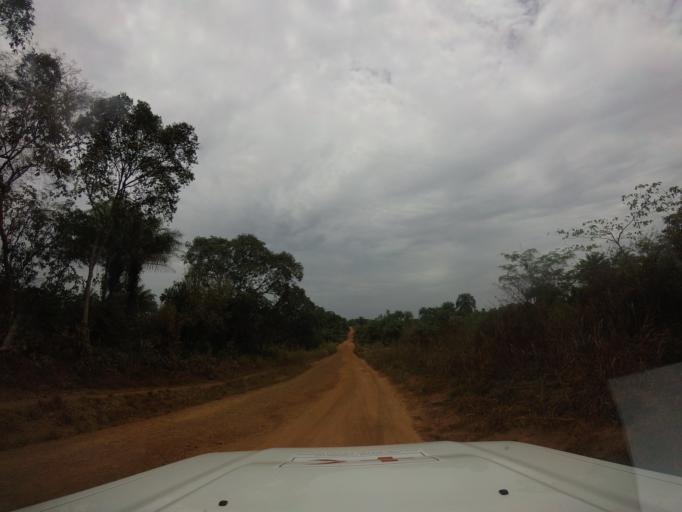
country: LR
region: Grand Cape Mount
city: Robertsport
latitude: 6.9407
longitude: -11.3282
